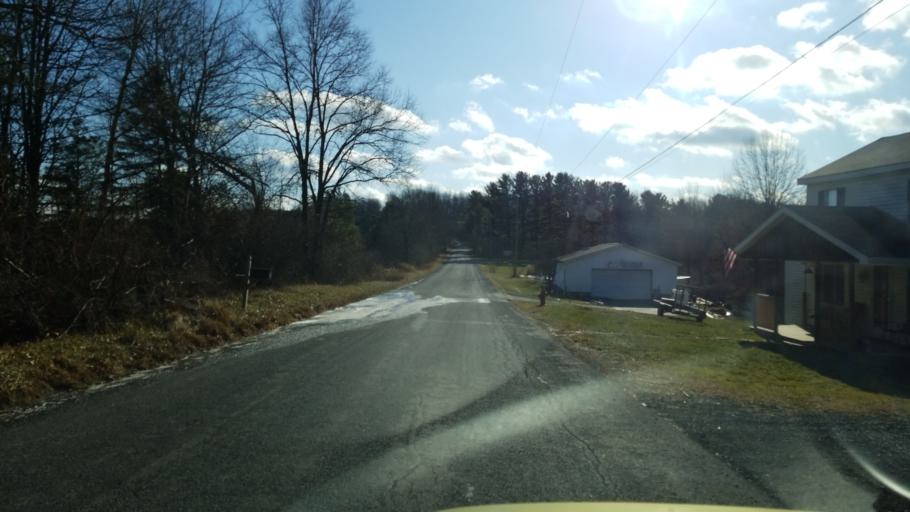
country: US
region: Pennsylvania
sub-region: Clearfield County
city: Clearfield
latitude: 41.0093
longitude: -78.4203
